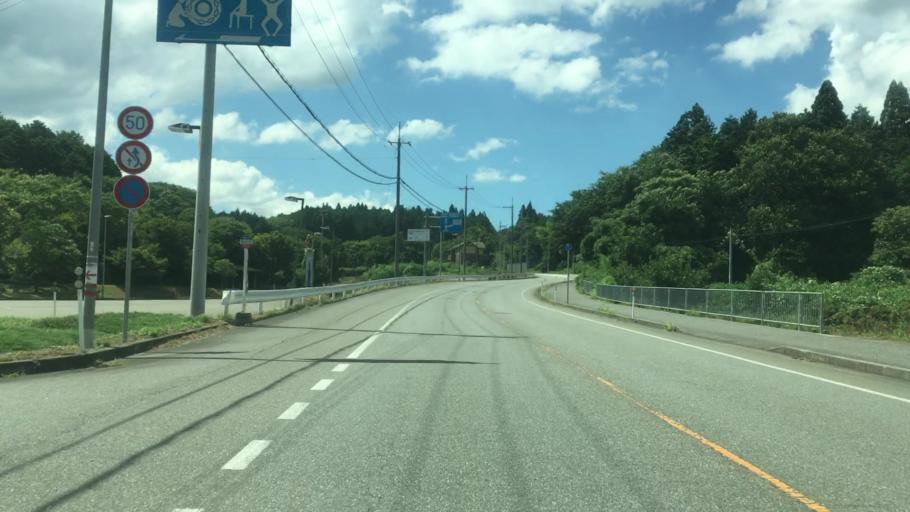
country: JP
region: Hyogo
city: Toyooka
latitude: 35.4843
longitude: 134.7056
